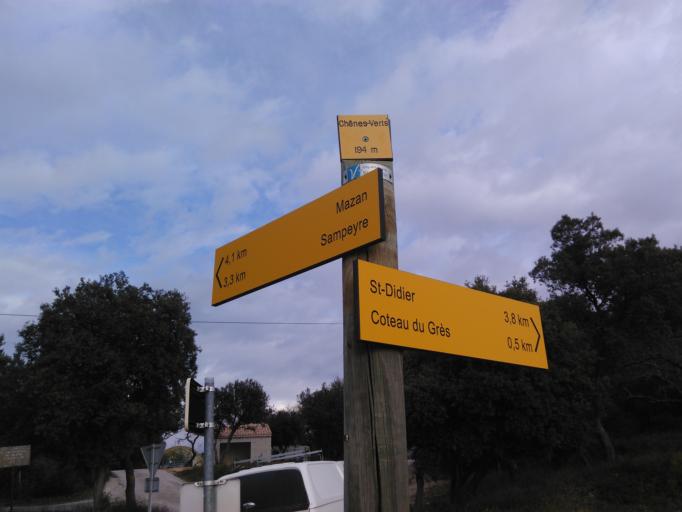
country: FR
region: Provence-Alpes-Cote d'Azur
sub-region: Departement du Vaucluse
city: Malemort-du-Comtat
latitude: 44.0236
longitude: 5.1324
